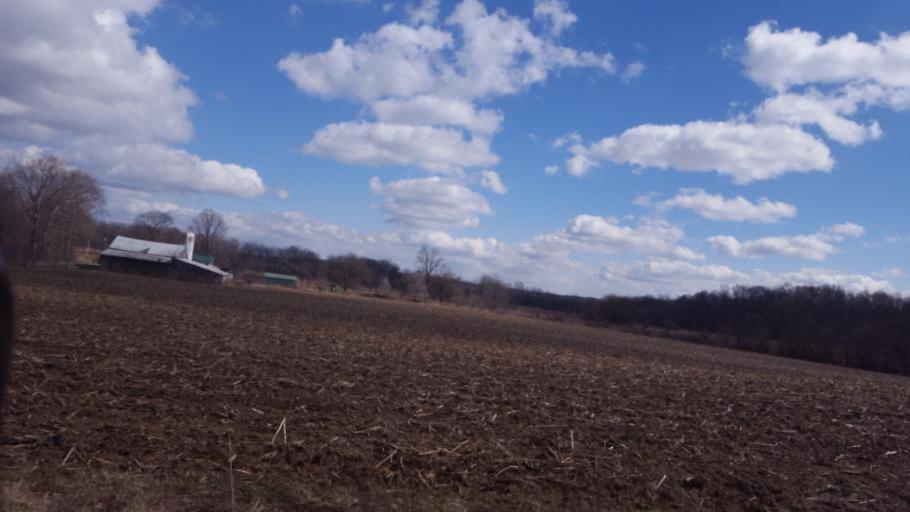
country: US
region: Ohio
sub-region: Knox County
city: Fredericktown
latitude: 40.5011
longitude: -82.5714
